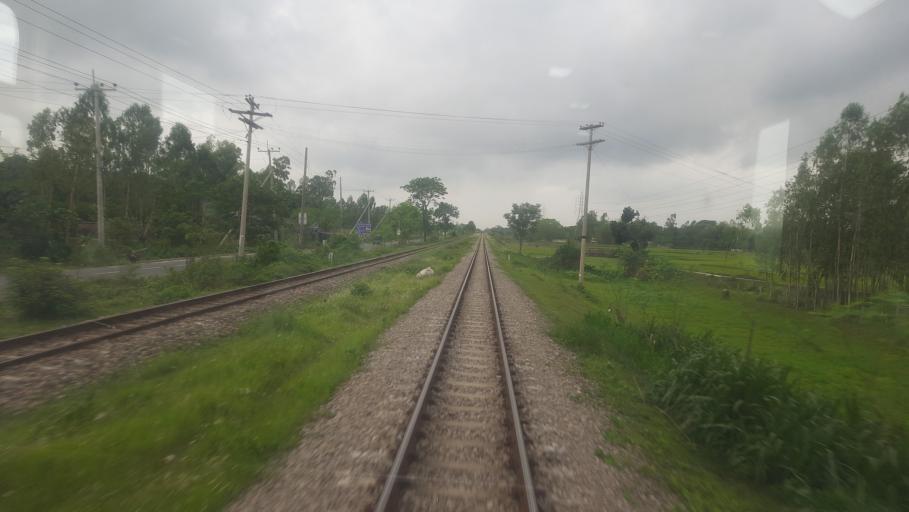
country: BD
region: Dhaka
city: Bhairab Bazar
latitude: 23.9843
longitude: 90.8496
